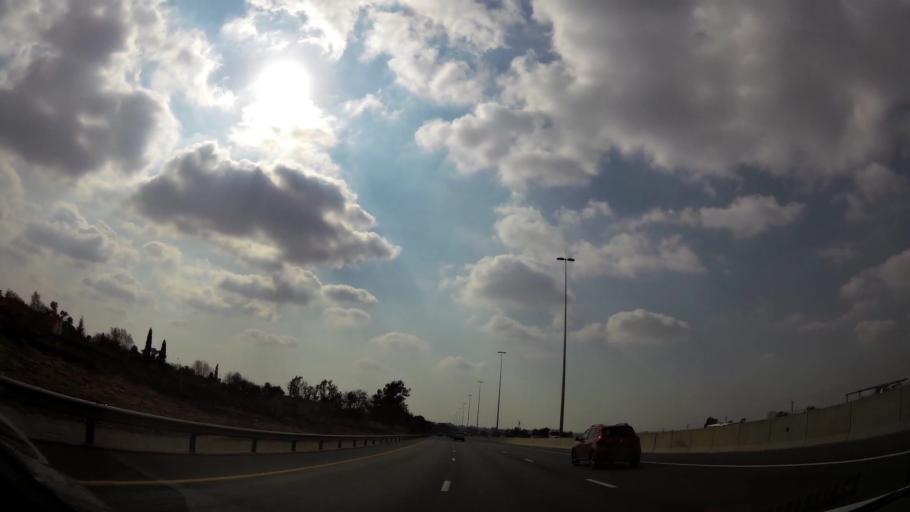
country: ZA
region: Gauteng
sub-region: Ekurhuleni Metropolitan Municipality
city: Benoni
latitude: -26.1675
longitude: 28.3543
